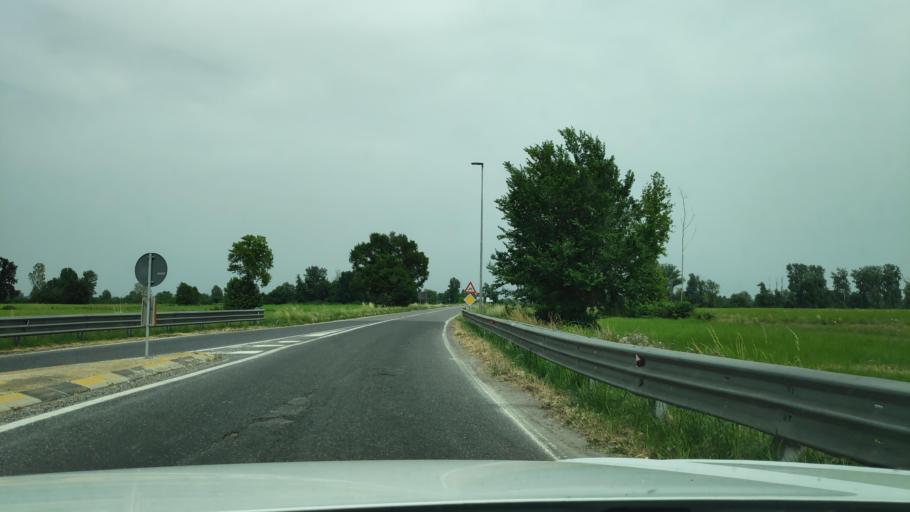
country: IT
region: Lombardy
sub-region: Provincia di Cremona
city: Campagnola Cremasca
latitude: 45.4073
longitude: 9.6610
